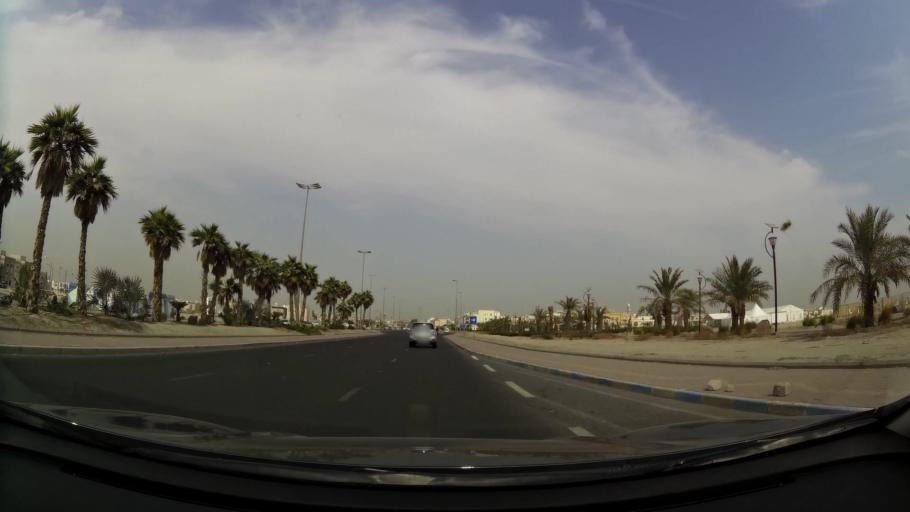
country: KW
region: Al Farwaniyah
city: Janub as Surrah
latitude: 29.2877
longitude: 48.0027
